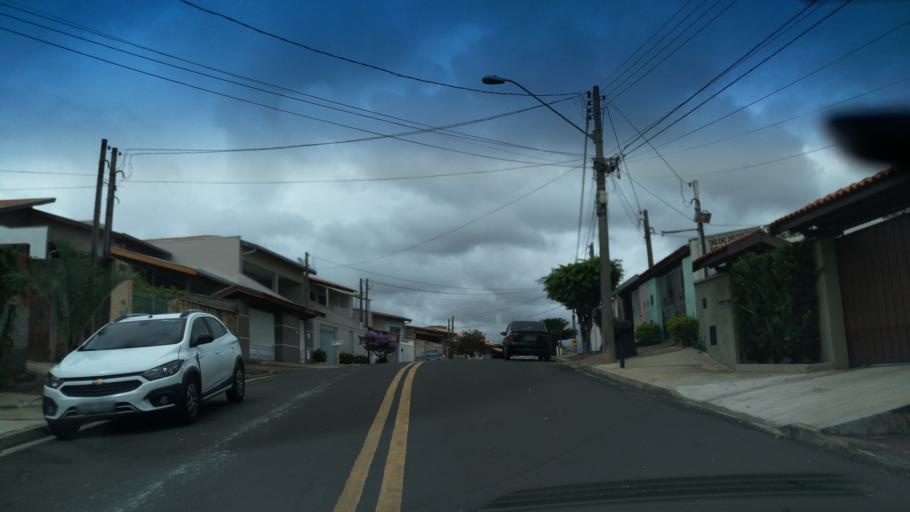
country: BR
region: Sao Paulo
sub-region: Valinhos
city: Valinhos
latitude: -22.9573
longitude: -46.9744
